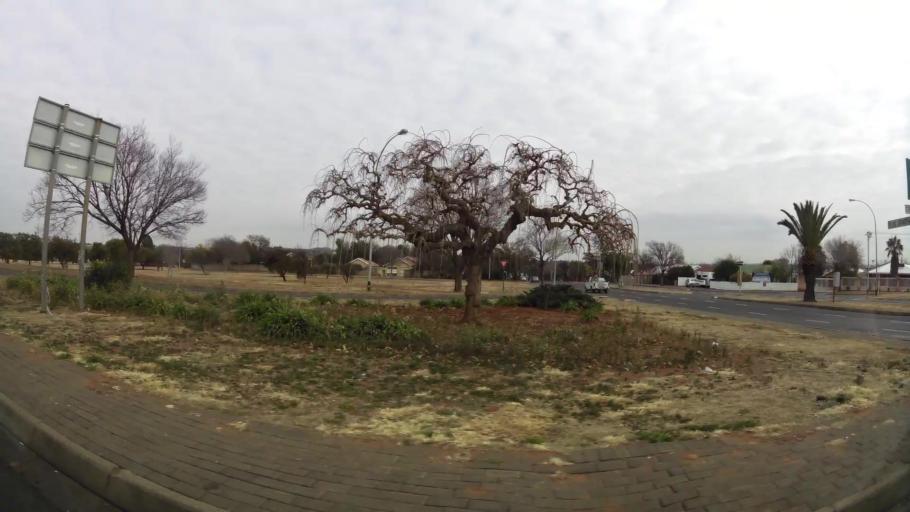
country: ZA
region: Orange Free State
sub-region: Mangaung Metropolitan Municipality
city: Bloemfontein
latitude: -29.1467
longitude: 26.1933
